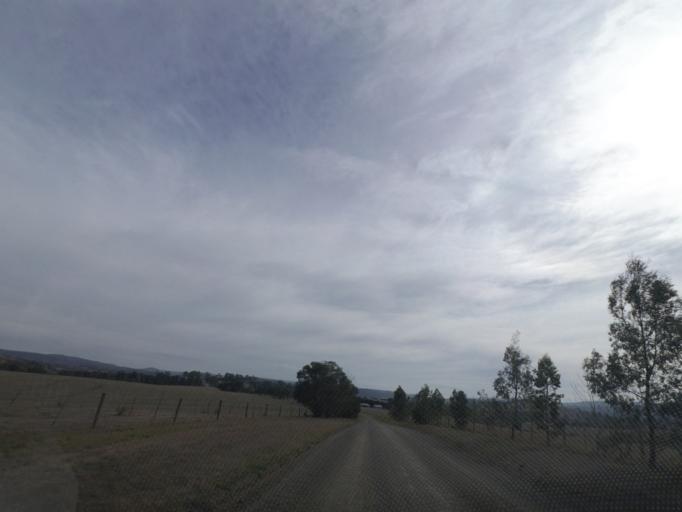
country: AU
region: Victoria
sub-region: Yarra Ranges
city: Yarra Glen
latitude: -37.6299
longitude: 145.4252
